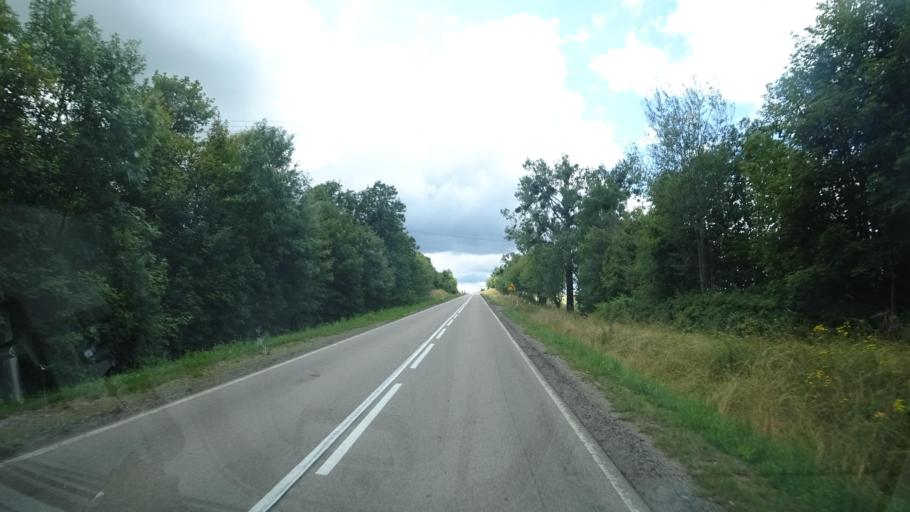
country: PL
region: Warmian-Masurian Voivodeship
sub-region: Powiat goldapski
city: Goldap
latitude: 54.2324
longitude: 22.2504
